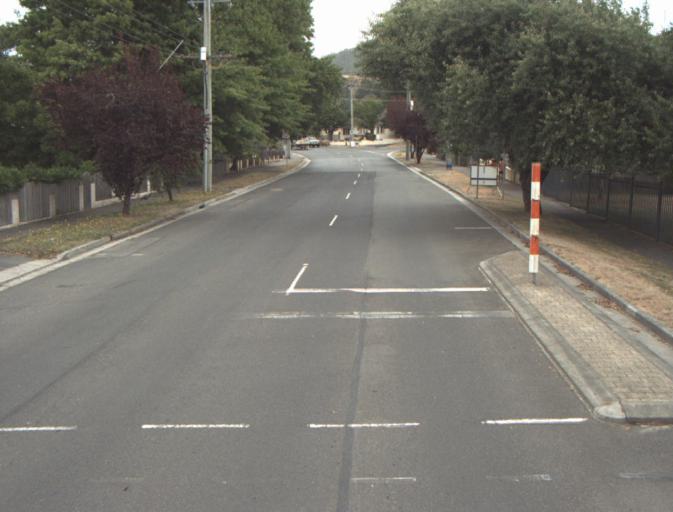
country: AU
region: Tasmania
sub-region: Launceston
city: Mayfield
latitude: -41.2525
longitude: 147.2161
